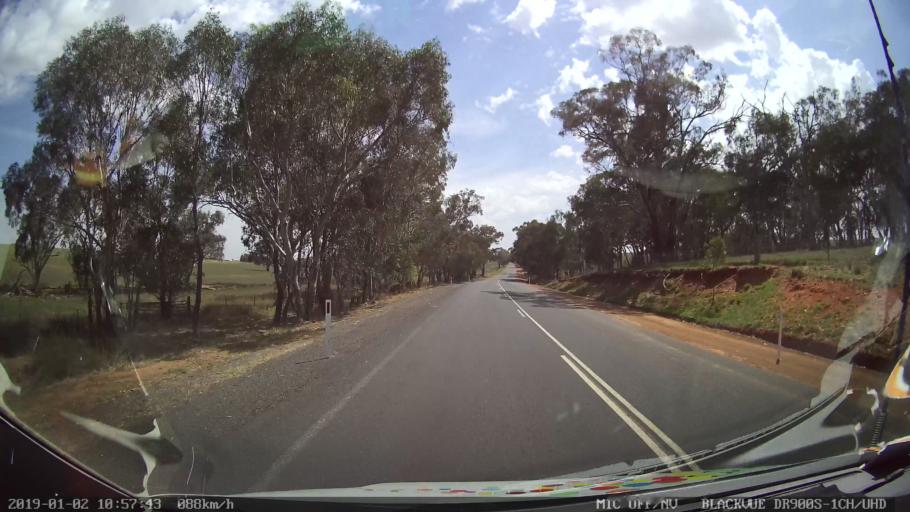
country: AU
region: New South Wales
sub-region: Cootamundra
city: Cootamundra
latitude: -34.6321
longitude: 148.2846
